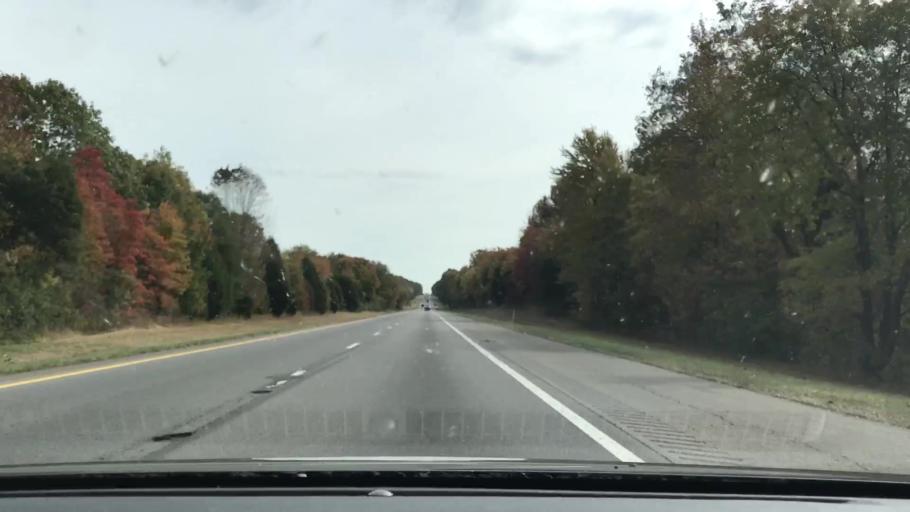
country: US
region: Tennessee
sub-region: Cheatham County
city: Pleasant View
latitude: 36.4284
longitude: -87.0672
